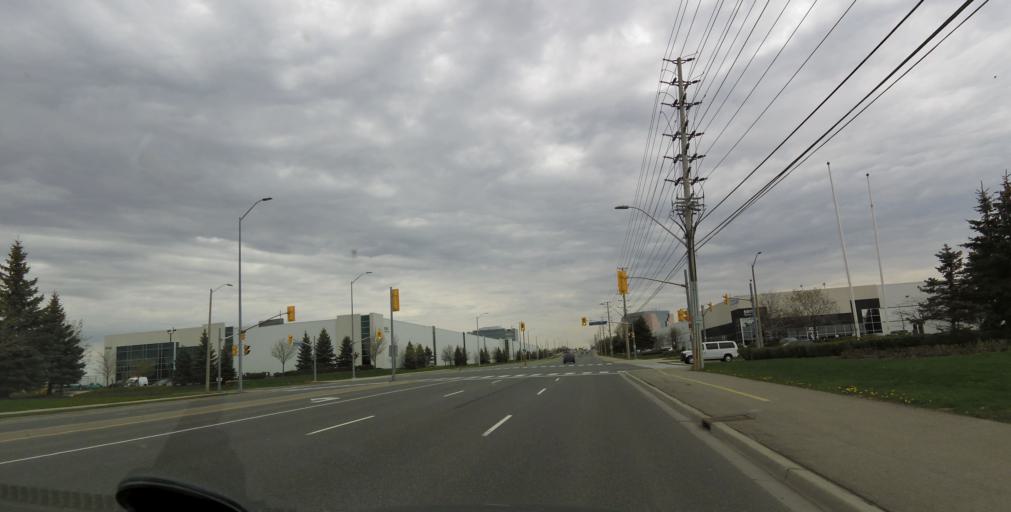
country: CA
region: Ontario
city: Mississauga
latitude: 43.6200
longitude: -79.6864
